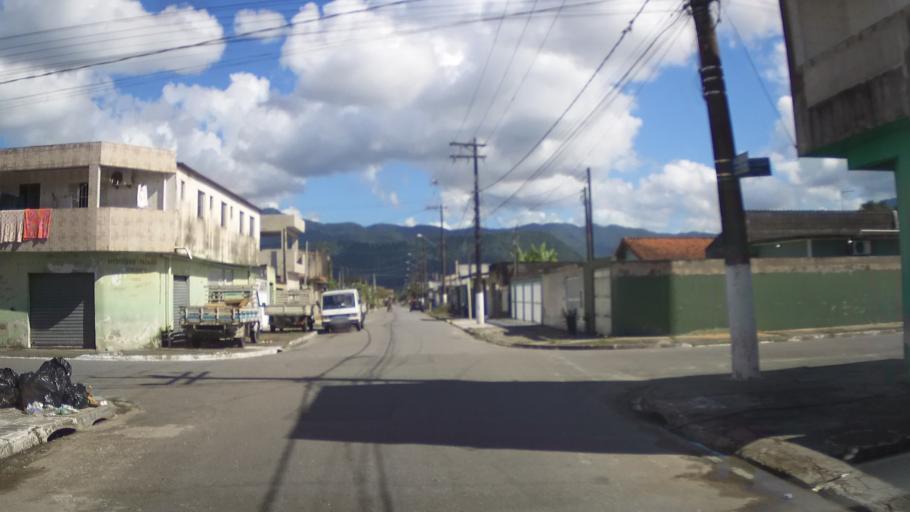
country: BR
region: Sao Paulo
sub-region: Praia Grande
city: Praia Grande
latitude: -24.0208
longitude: -46.5083
